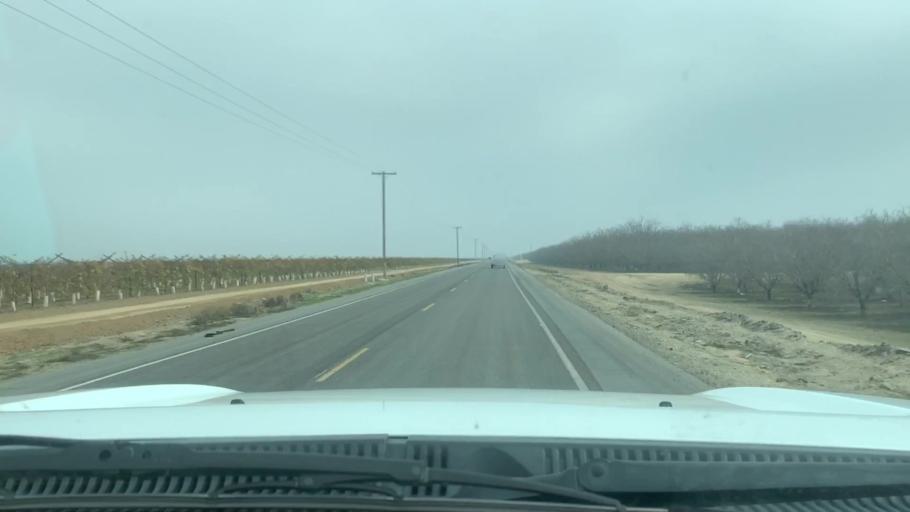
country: US
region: California
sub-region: Kern County
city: Buttonwillow
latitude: 35.5005
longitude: -119.4356
